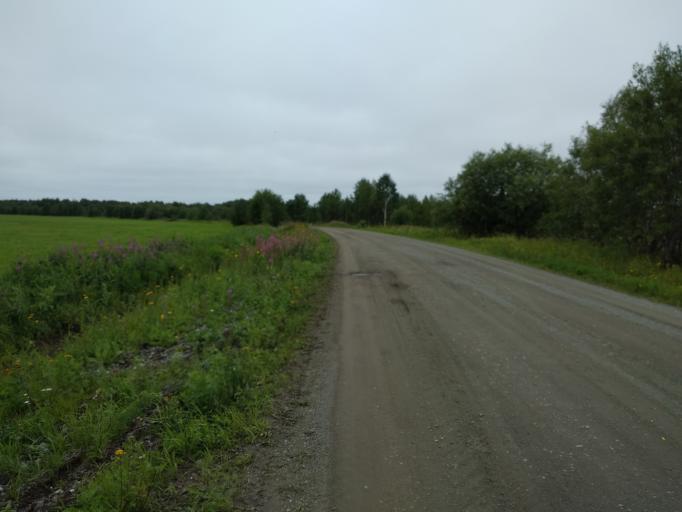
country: RU
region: Sverdlovsk
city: Serov
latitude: 59.8483
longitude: 60.5811
